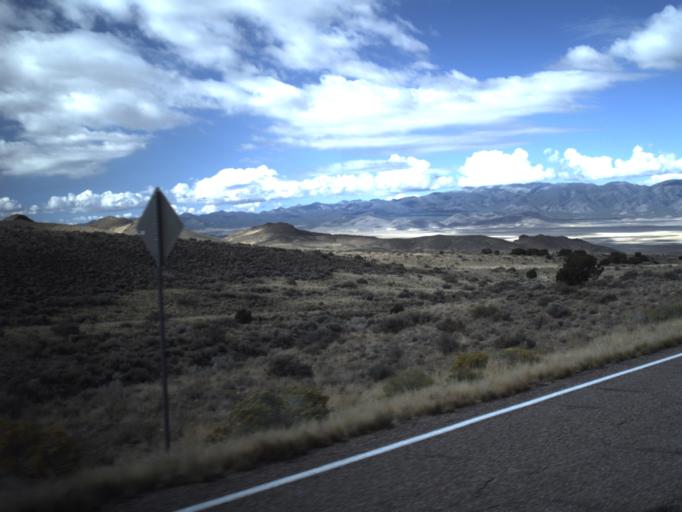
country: US
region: Utah
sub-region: Beaver County
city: Milford
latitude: 38.4345
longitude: -113.2916
